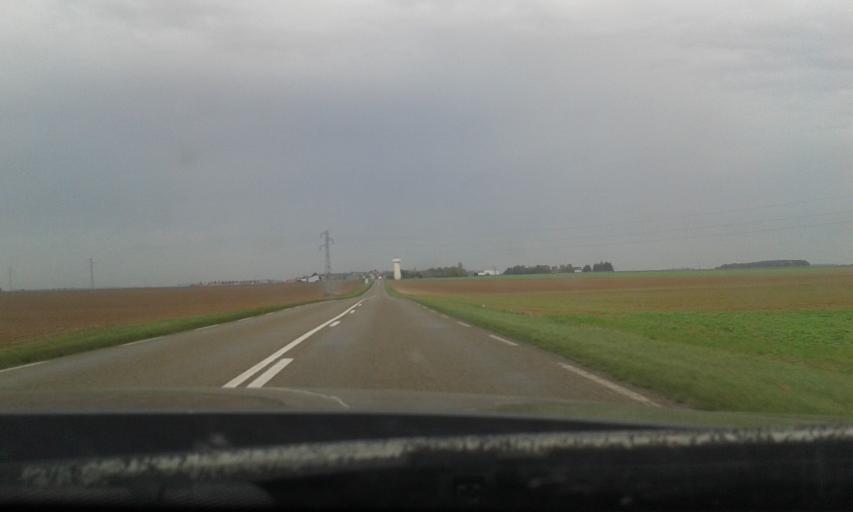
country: FR
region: Centre
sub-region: Departement d'Eure-et-Loir
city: Janville
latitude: 48.1938
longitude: 1.8282
